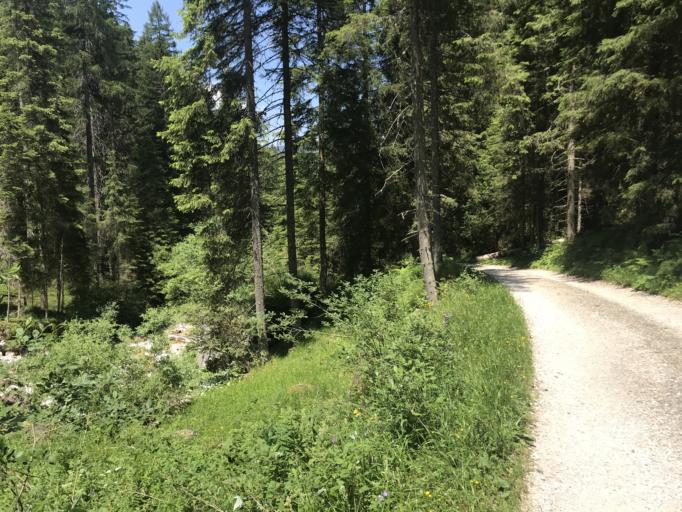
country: IT
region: Trentino-Alto Adige
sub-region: Bolzano
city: San Pietro
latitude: 46.6255
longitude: 11.7344
